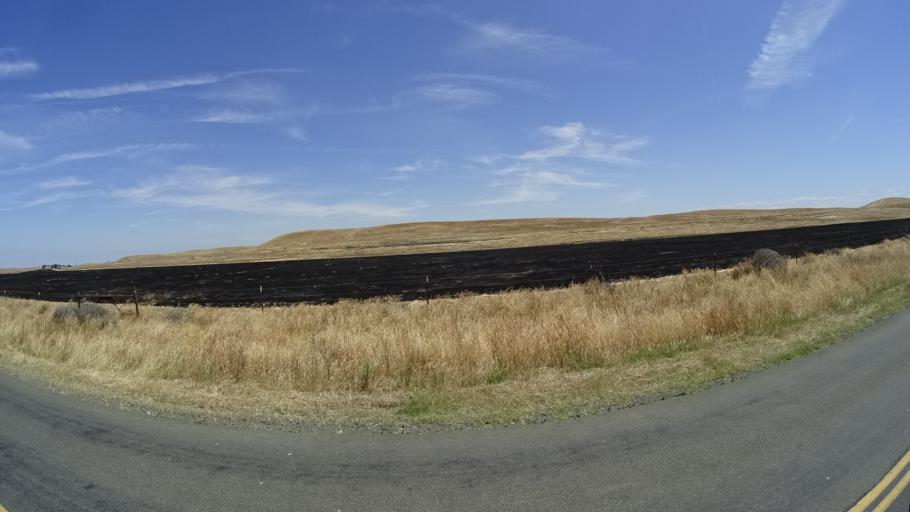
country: US
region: California
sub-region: Kings County
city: Kettleman City
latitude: 35.8342
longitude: -119.9152
